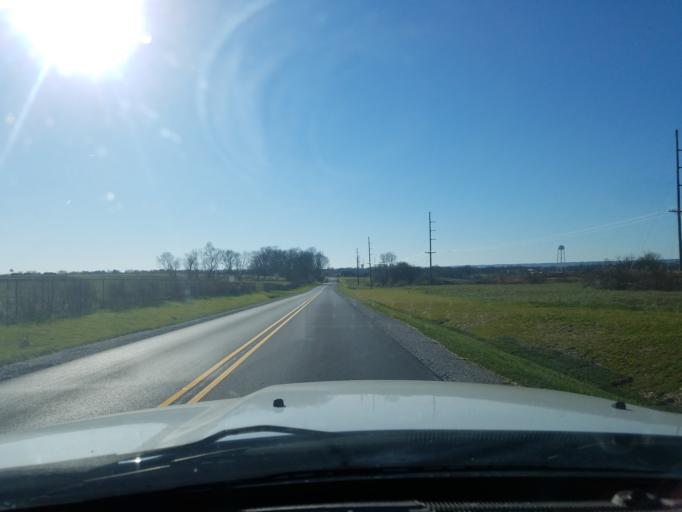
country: US
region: Kentucky
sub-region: Jefferson County
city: Prospect
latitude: 38.3641
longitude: -85.6722
